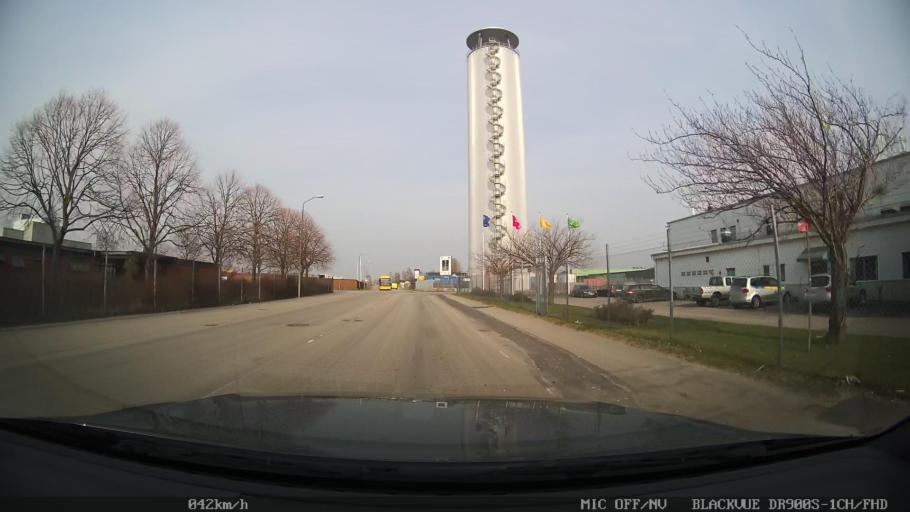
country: SE
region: Skane
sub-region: Ystads Kommun
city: Ystad
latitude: 55.4409
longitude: 13.8413
